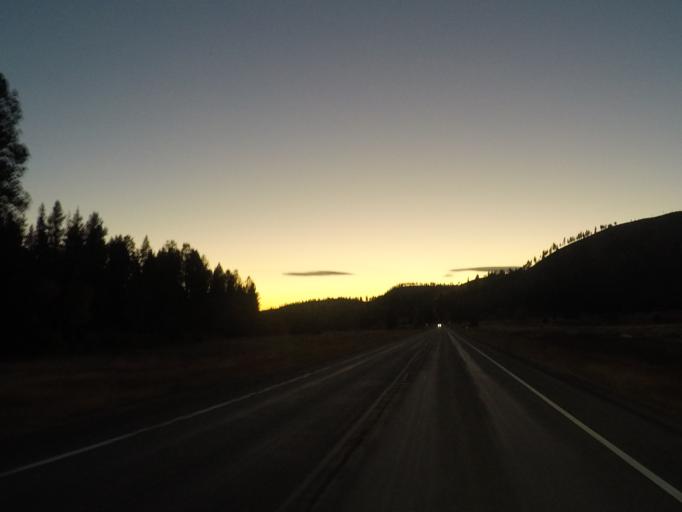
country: US
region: Montana
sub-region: Missoula County
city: Seeley Lake
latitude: 47.0305
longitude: -113.2665
